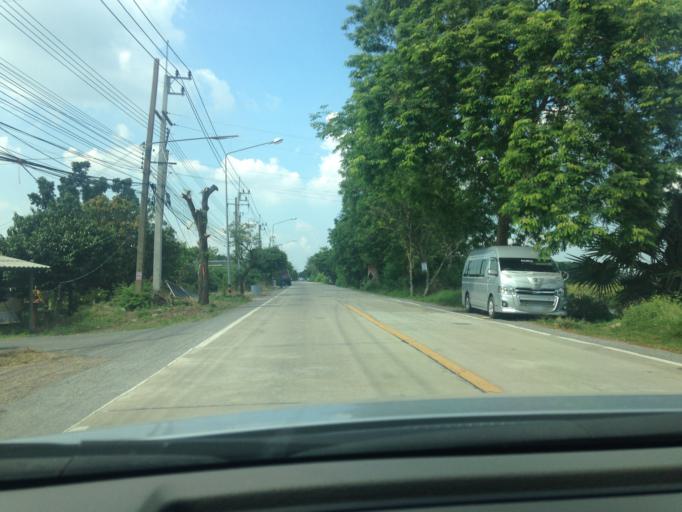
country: TH
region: Phra Nakhon Si Ayutthaya
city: Ban Bang Kadi Pathum Thani
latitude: 13.9906
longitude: 100.5988
